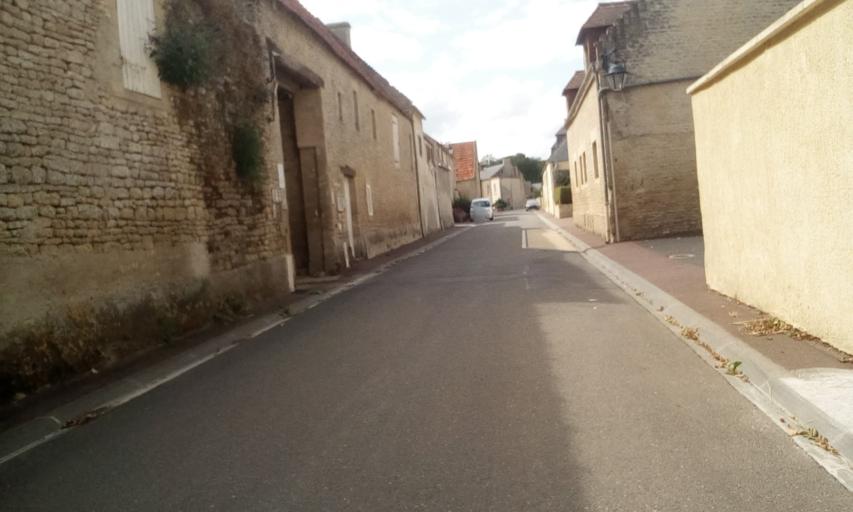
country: FR
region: Lower Normandy
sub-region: Departement du Calvados
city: Courseulles-sur-Mer
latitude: 49.3120
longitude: -0.4842
